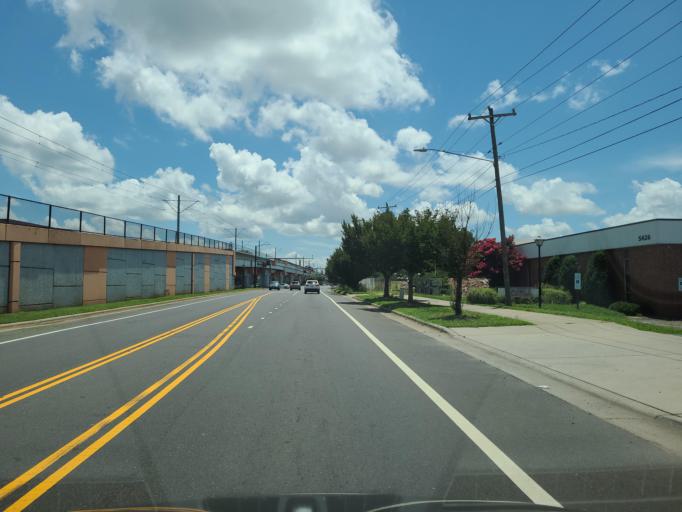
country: US
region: North Carolina
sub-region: Mecklenburg County
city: Charlotte
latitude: 35.1667
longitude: -80.8778
